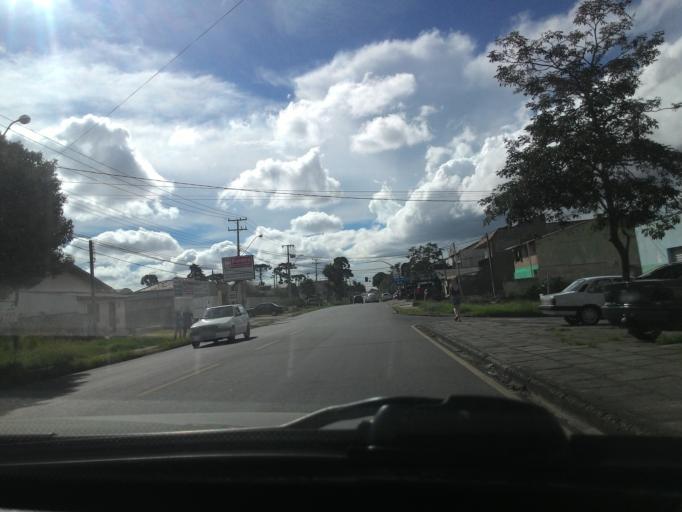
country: BR
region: Parana
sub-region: Sao Jose Dos Pinhais
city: Sao Jose dos Pinhais
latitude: -25.5177
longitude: -49.1912
